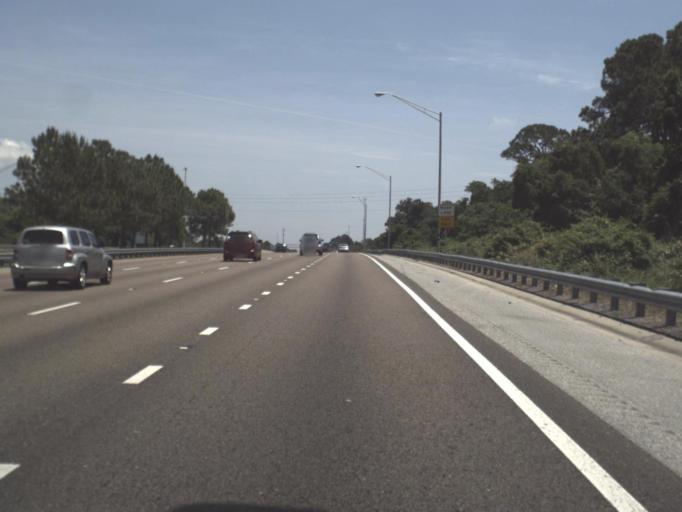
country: US
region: Florida
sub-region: Clay County
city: Orange Park
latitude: 30.1847
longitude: -81.6374
